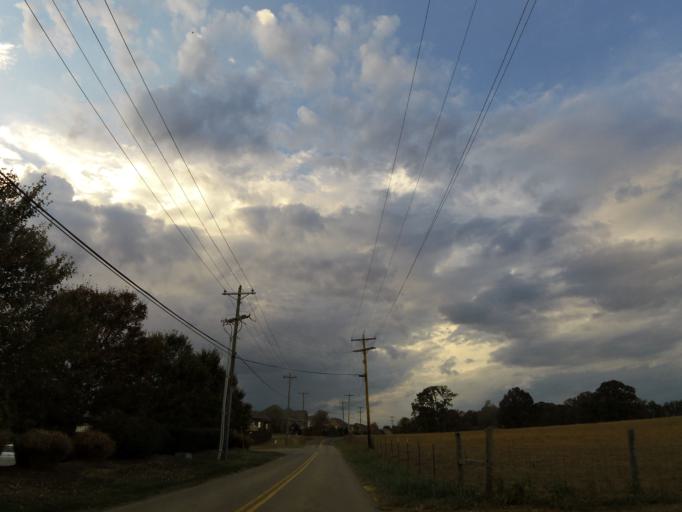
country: US
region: Tennessee
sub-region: Blount County
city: Maryville
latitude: 35.7667
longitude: -84.0253
